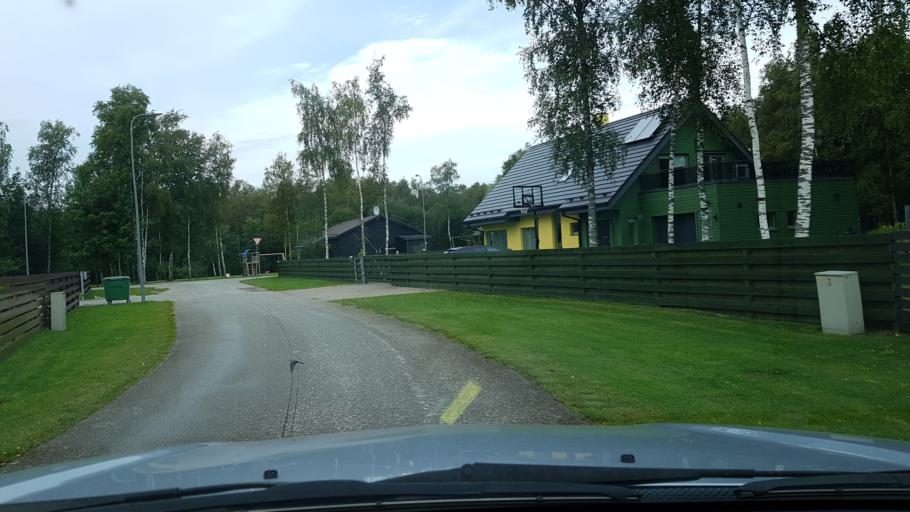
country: EE
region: Harju
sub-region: Rae vald
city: Jueri
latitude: 59.3763
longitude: 24.9418
